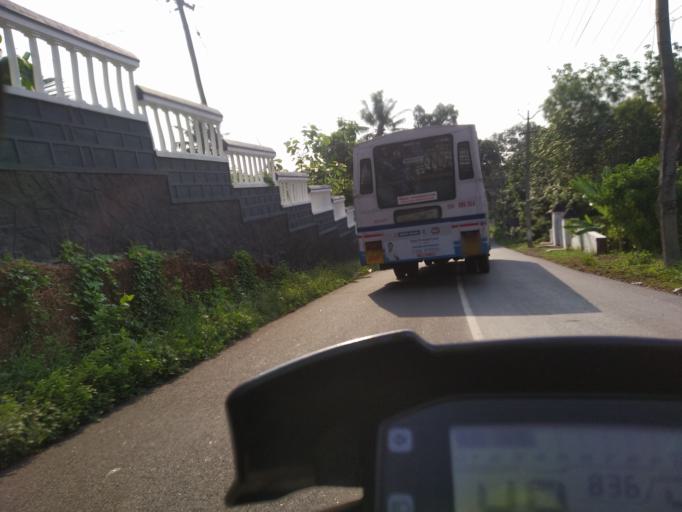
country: IN
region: Kerala
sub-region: Ernakulam
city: Ramamangalam
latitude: 9.9145
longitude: 76.4288
